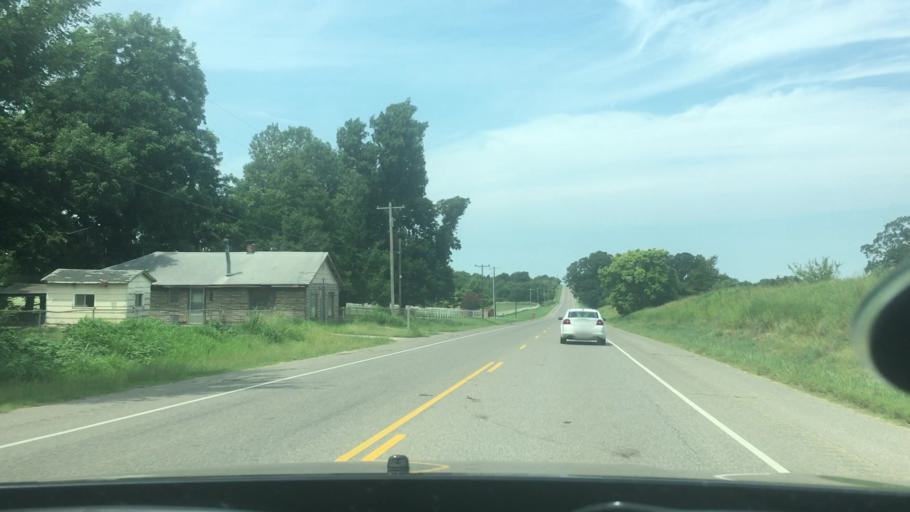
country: US
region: Oklahoma
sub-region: Pottawatomie County
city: Shawnee
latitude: 35.3331
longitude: -96.8250
